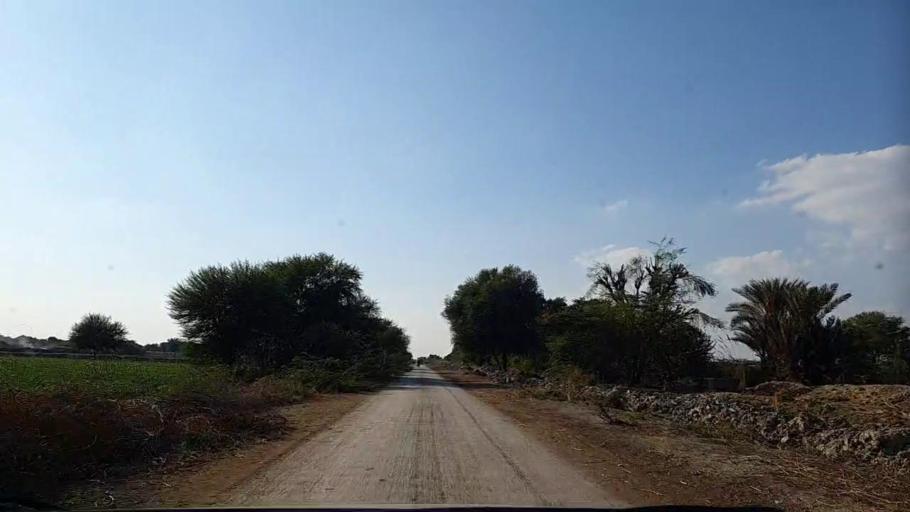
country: PK
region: Sindh
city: Pithoro
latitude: 25.6463
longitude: 69.3449
